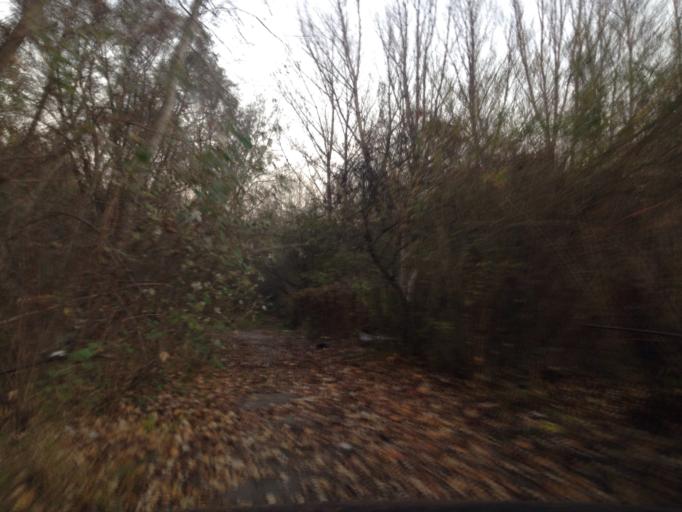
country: PL
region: Masovian Voivodeship
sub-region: Warszawa
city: Wlochy
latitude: 52.1600
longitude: 20.9583
